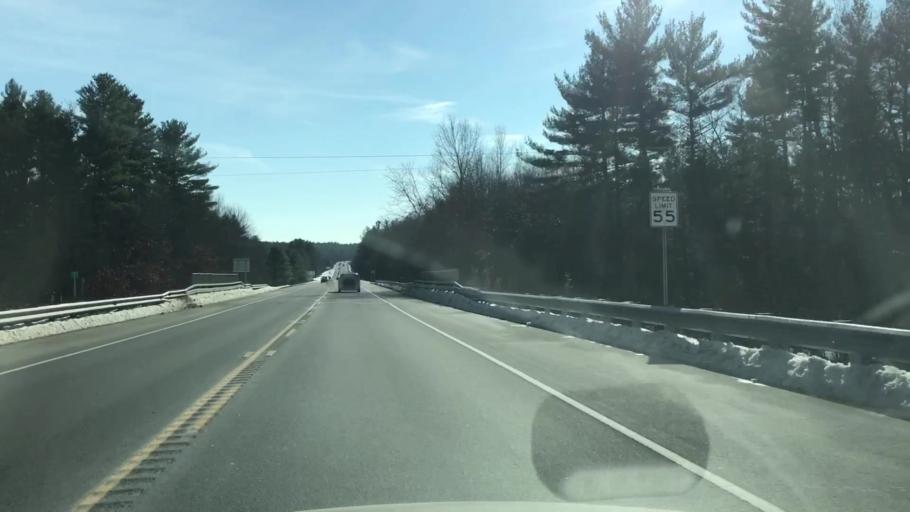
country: US
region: New Hampshire
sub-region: Hillsborough County
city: Milford
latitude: 42.8369
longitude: -71.6191
